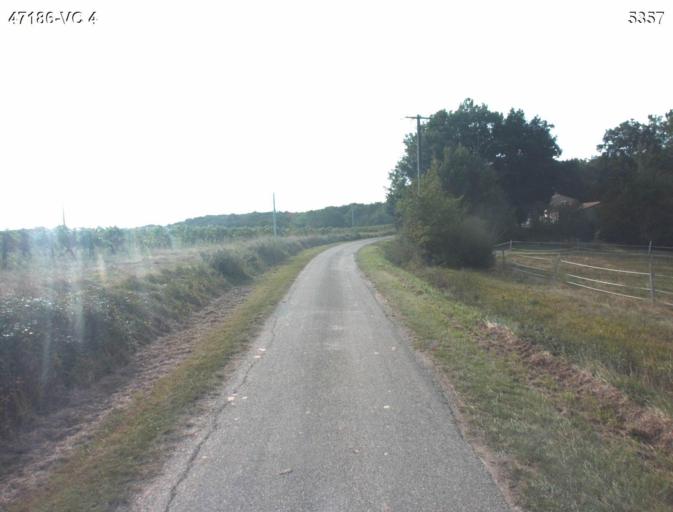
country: FR
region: Aquitaine
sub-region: Departement du Lot-et-Garonne
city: Sainte-Colombe-en-Bruilhois
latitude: 44.1881
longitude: 0.4590
